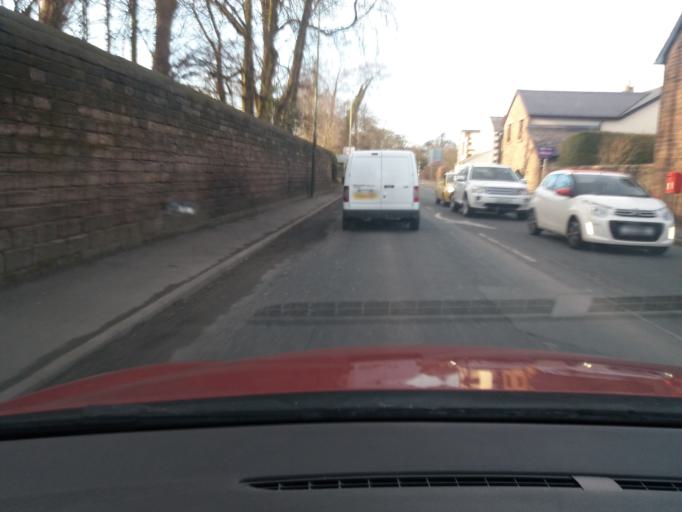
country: GB
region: England
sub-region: Lancashire
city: Euxton
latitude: 53.6595
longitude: -2.6744
